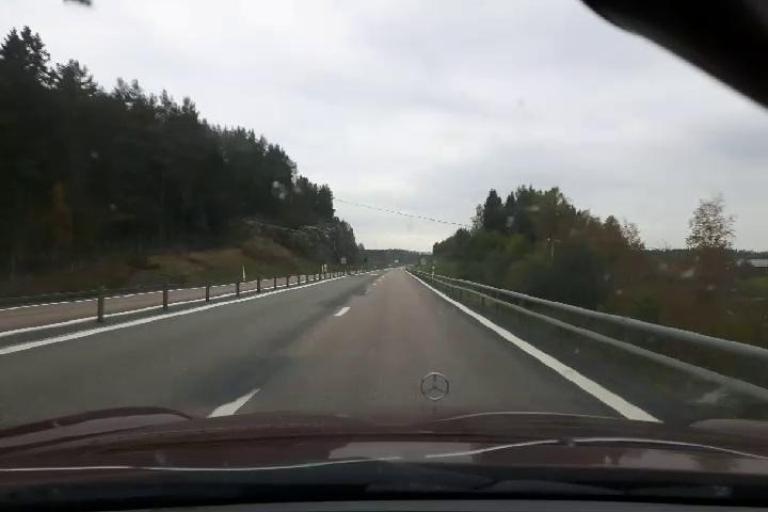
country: SE
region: Vaesternorrland
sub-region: Kramfors Kommun
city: Nordingra
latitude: 62.9253
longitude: 18.0987
